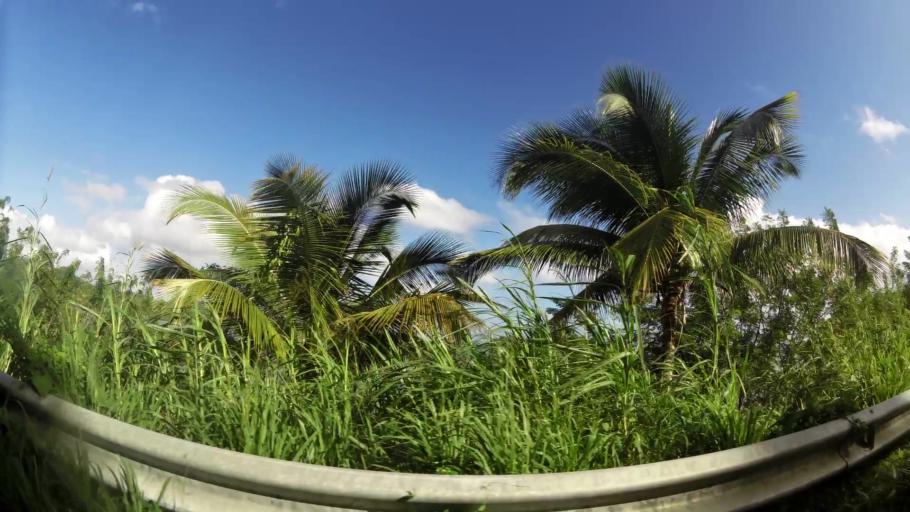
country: MQ
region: Martinique
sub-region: Martinique
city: Le Francois
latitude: 14.6197
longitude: -60.8917
